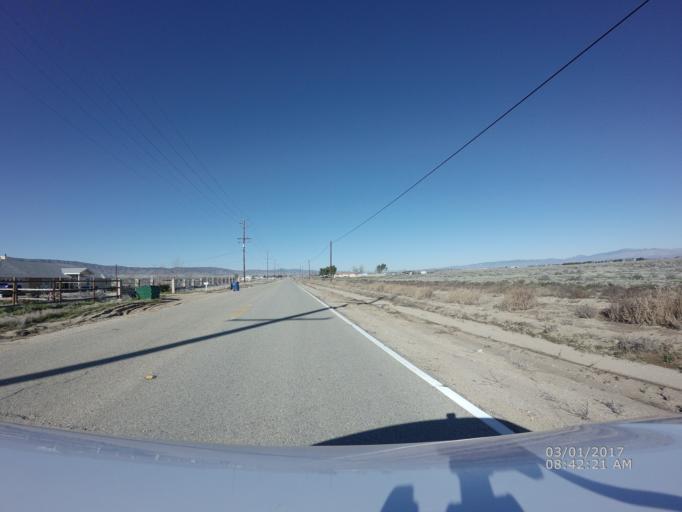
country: US
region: California
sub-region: Los Angeles County
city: Quartz Hill
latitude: 34.6894
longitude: -118.2655
